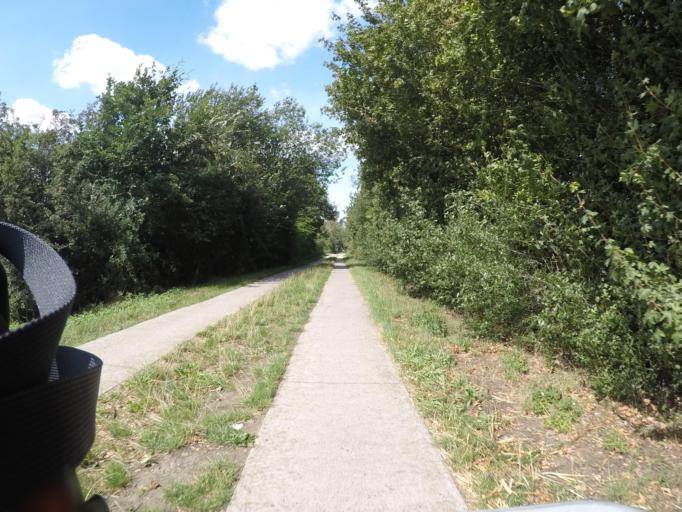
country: DE
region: Lower Saxony
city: Stelle
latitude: 53.4546
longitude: 10.1188
